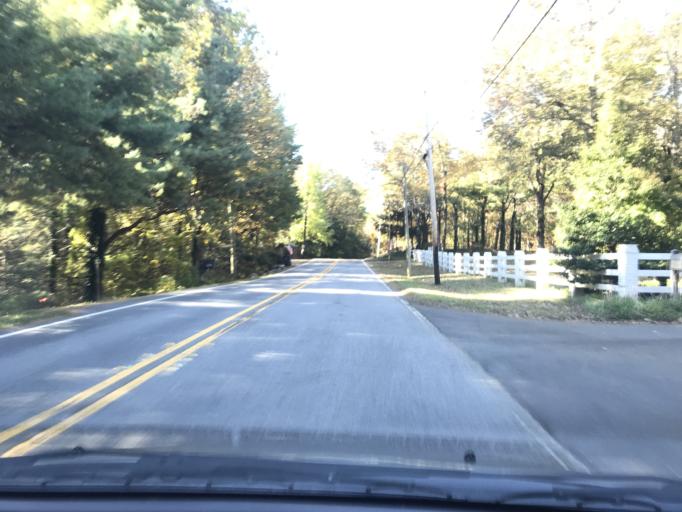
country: US
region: Georgia
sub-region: Walker County
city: Lookout Mountain
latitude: 34.9742
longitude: -85.3686
